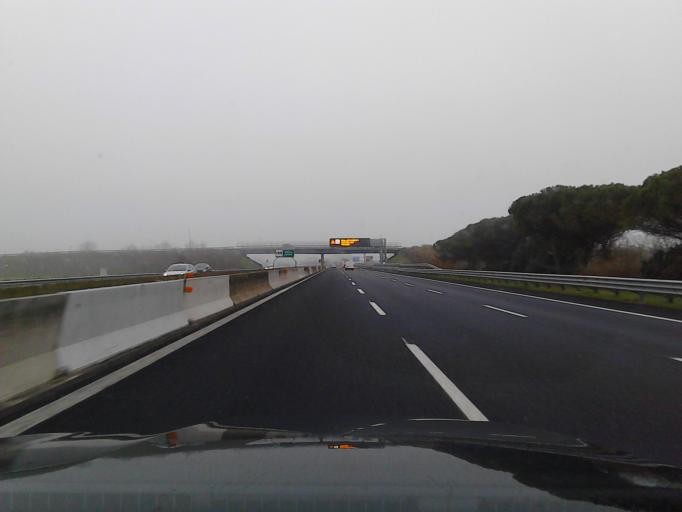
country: IT
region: Emilia-Romagna
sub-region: Forli-Cesena
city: Gatteo-Sant'Angelo
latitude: 44.1253
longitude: 12.3825
